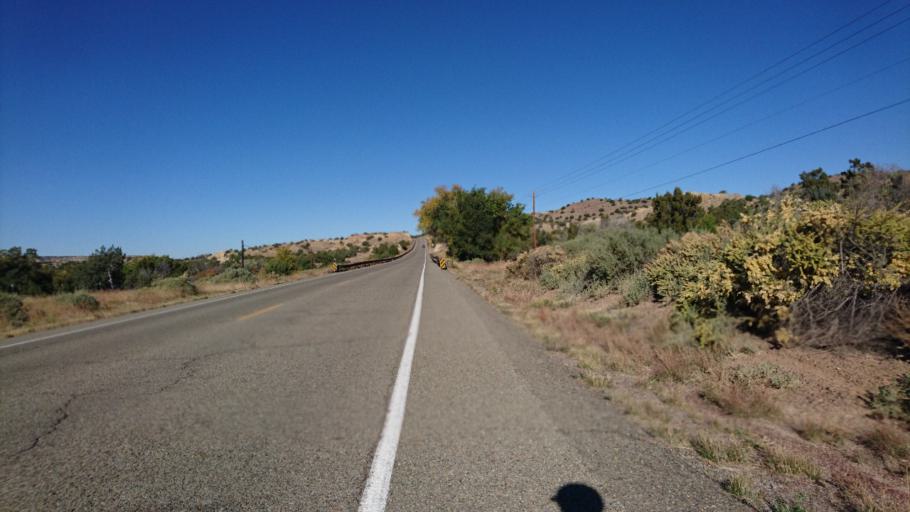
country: US
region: New Mexico
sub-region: Santa Fe County
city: La Cienega
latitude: 35.4320
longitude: -106.1001
